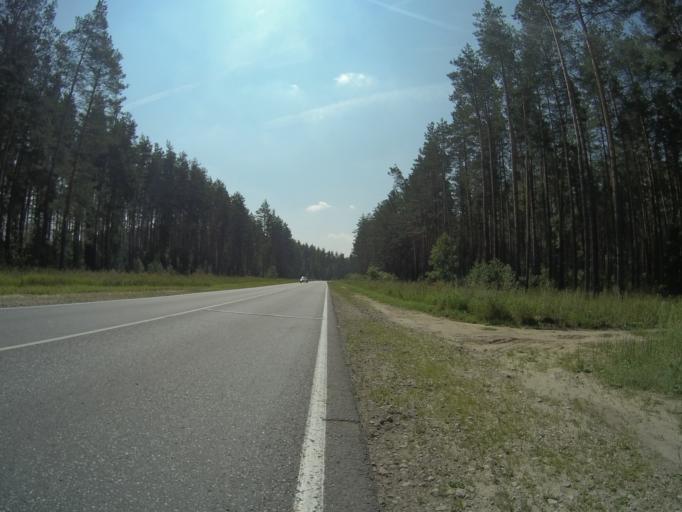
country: RU
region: Vladimir
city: Anopino
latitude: 55.6981
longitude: 40.7486
